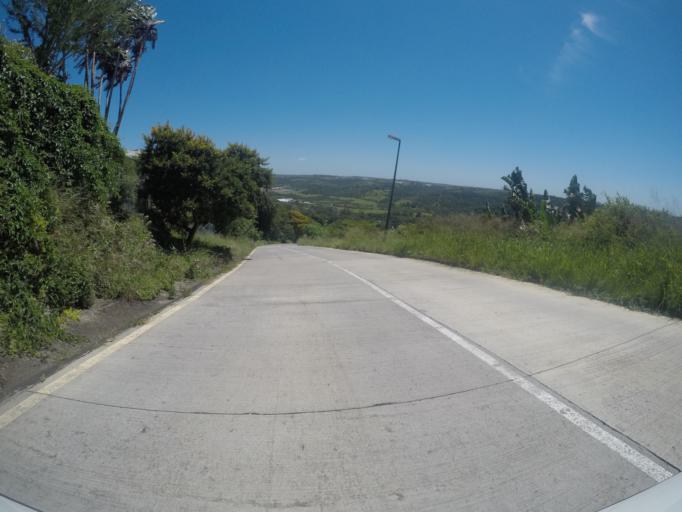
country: ZA
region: Eastern Cape
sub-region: Buffalo City Metropolitan Municipality
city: East London
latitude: -32.9319
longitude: 27.9945
